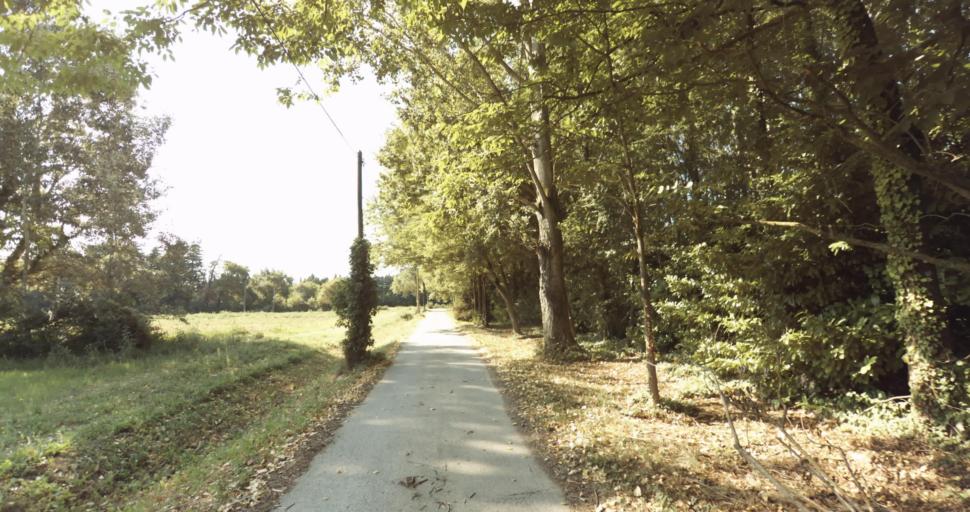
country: FR
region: Provence-Alpes-Cote d'Azur
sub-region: Departement du Vaucluse
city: Althen-des-Paluds
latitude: 44.0202
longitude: 4.9544
